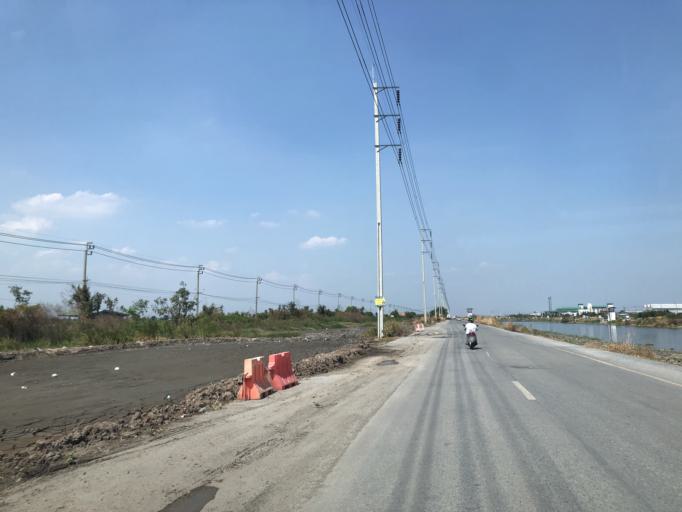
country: TH
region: Samut Prakan
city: Bang Bo District
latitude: 13.5150
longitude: 100.7458
